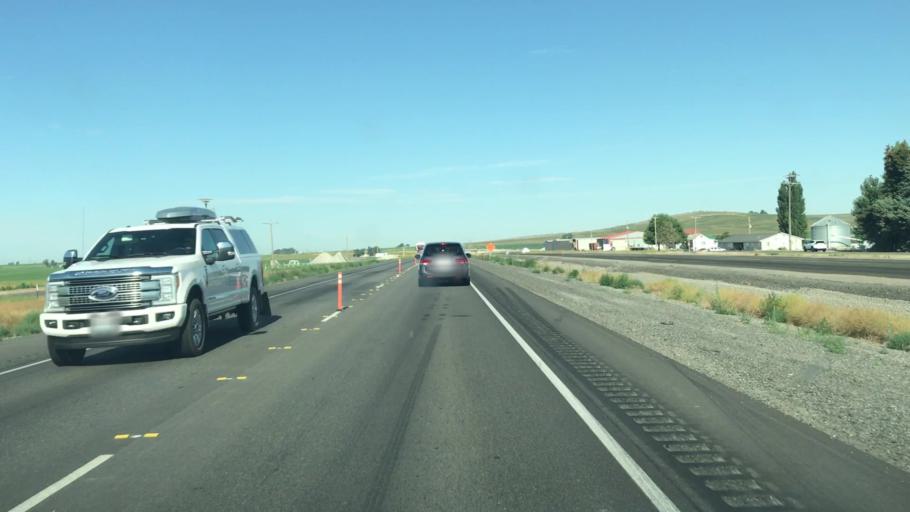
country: US
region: Idaho
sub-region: Twin Falls County
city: Hansen
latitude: 42.5759
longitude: -114.1891
